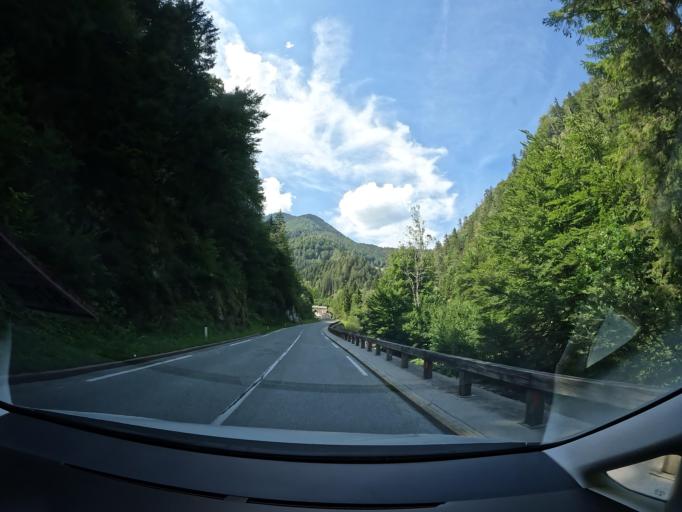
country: SI
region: Zirovnica
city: Zirovnica
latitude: 46.4324
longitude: 14.2284
